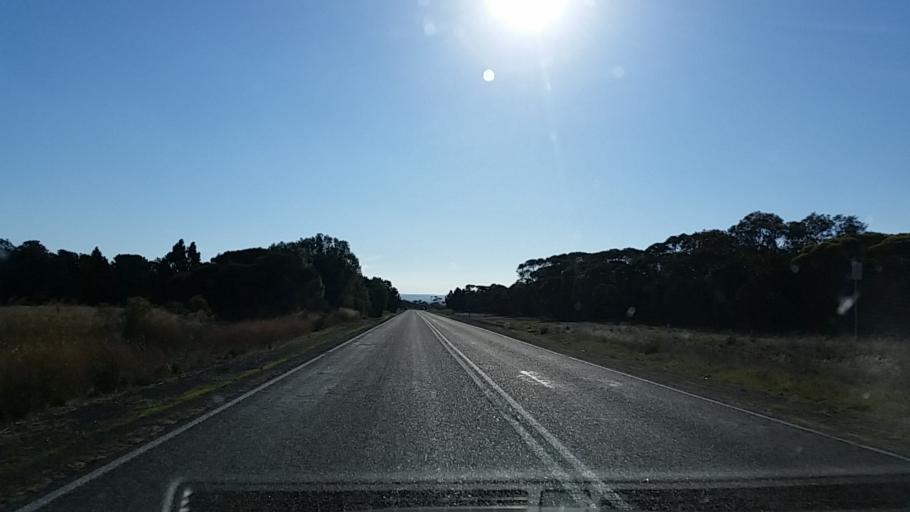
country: AU
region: South Australia
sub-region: Murray Bridge
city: Murray Bridge
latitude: -35.1326
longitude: 139.1963
